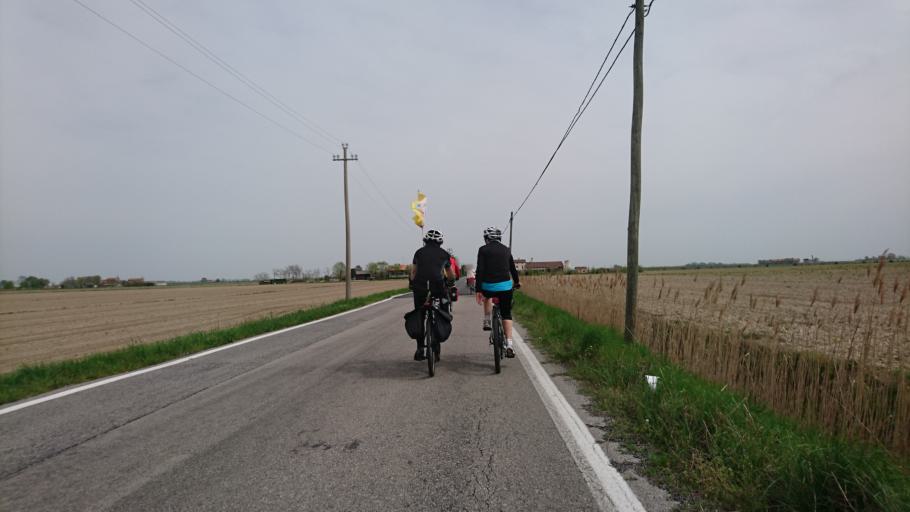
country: IT
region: Veneto
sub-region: Provincia di Venezia
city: La Salute di Livenza
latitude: 45.6580
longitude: 12.8346
